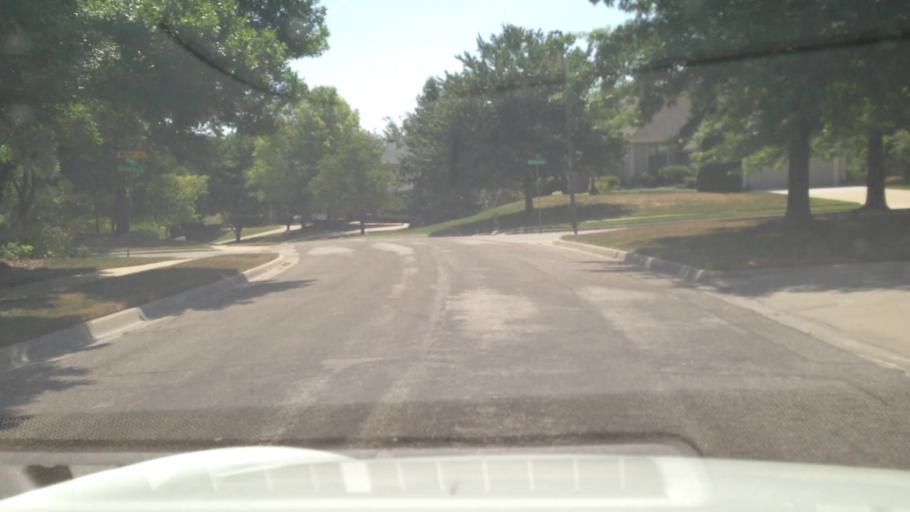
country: US
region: Kansas
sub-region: Douglas County
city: Lawrence
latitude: 38.9463
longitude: -95.3025
